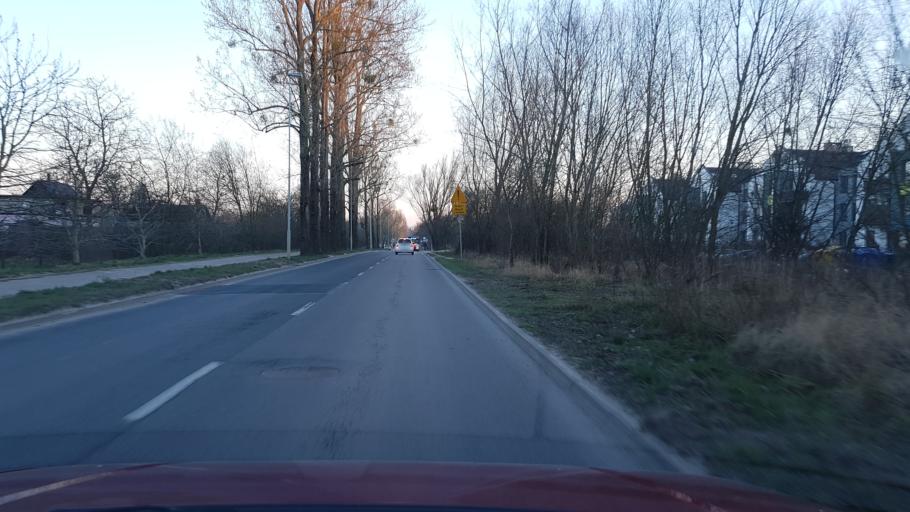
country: PL
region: West Pomeranian Voivodeship
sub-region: Szczecin
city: Szczecin
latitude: 53.4796
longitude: 14.5440
